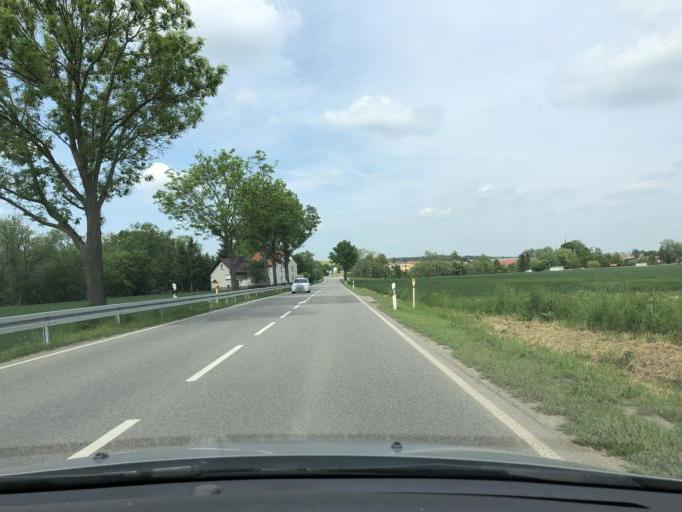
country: DE
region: Thuringia
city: Saara
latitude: 50.9470
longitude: 12.4250
